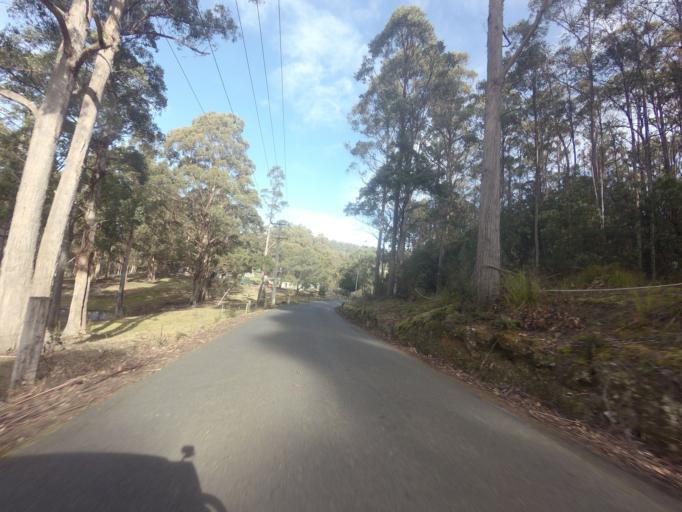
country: AU
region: Tasmania
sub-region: Kingborough
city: Margate
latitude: -43.0112
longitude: 147.1656
